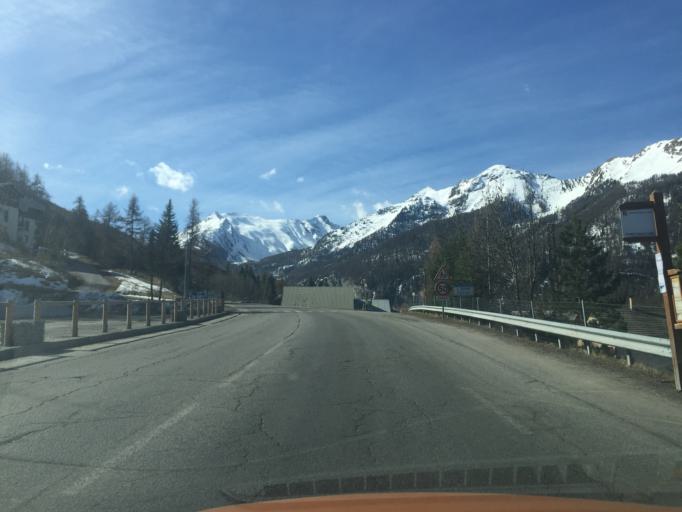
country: FR
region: Provence-Alpes-Cote d'Azur
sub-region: Departement des Hautes-Alpes
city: Embrun
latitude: 44.4969
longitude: 6.5547
